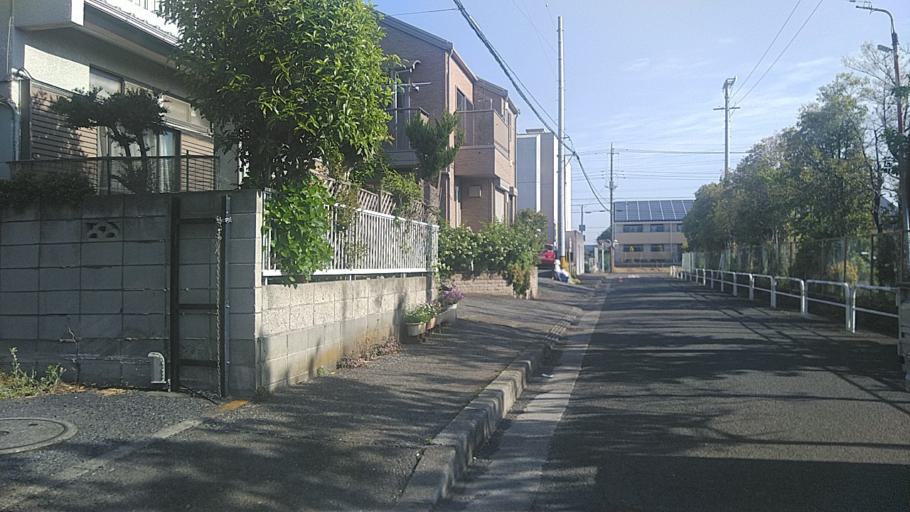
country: JP
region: Saitama
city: Wako
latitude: 35.7949
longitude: 139.6365
